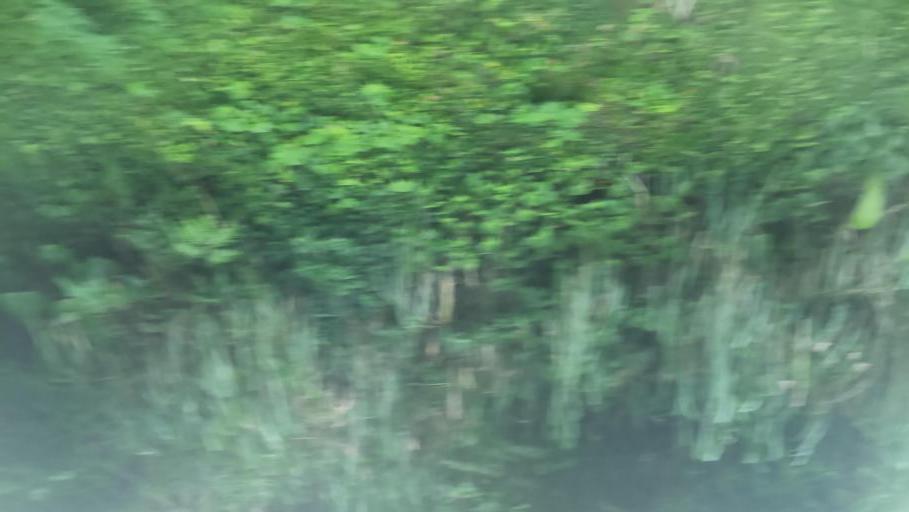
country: TW
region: Taipei
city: Taipei
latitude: 25.1388
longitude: 121.6031
